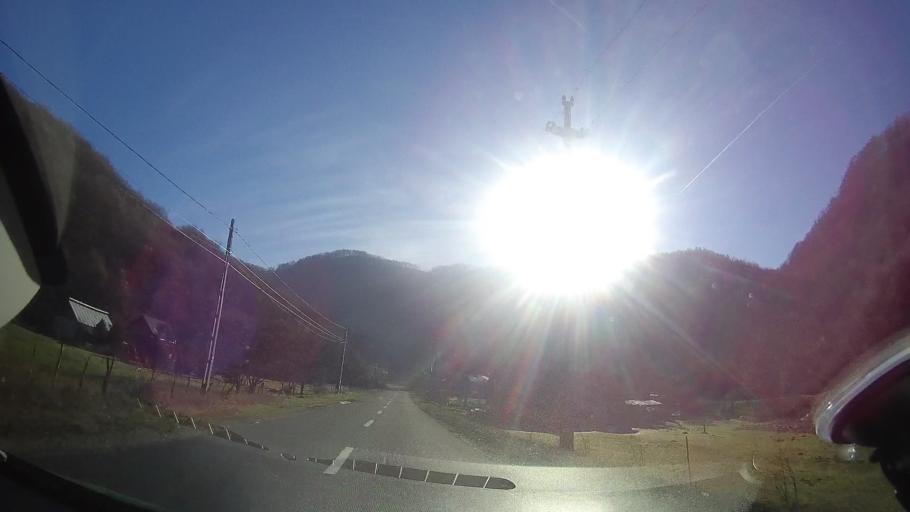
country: RO
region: Bihor
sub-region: Comuna Bulz
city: Bulz
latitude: 46.9189
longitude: 22.6547
